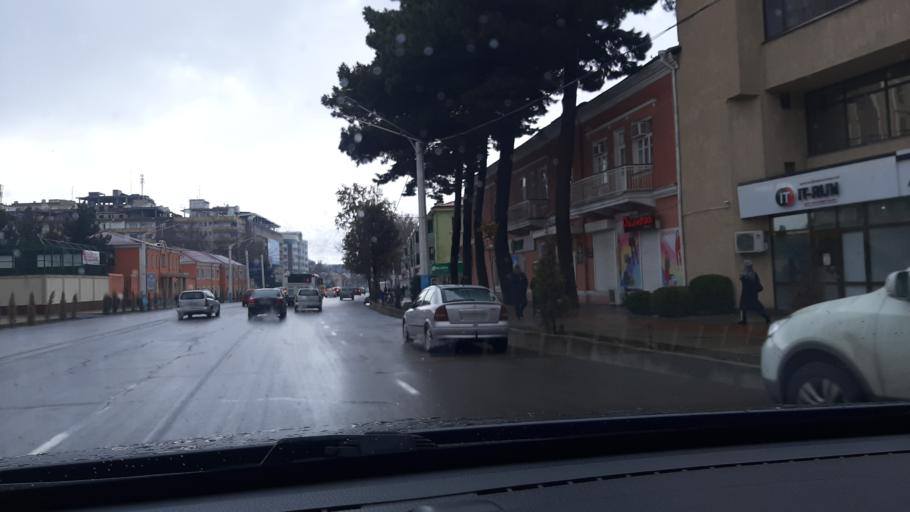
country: TJ
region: Viloyati Sughd
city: Khujand
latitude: 40.2804
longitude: 69.6261
